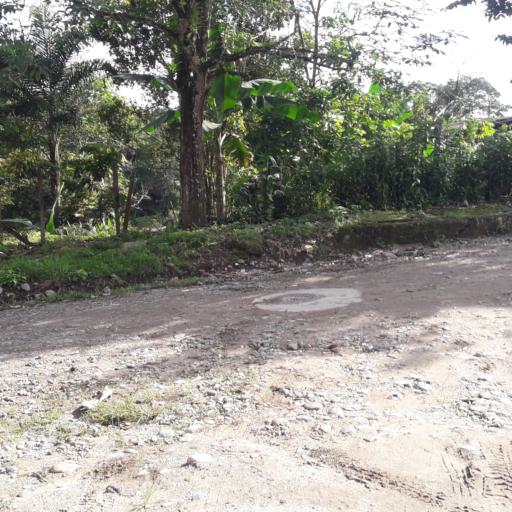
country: EC
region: Napo
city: Tena
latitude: -0.9974
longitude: -77.8156
